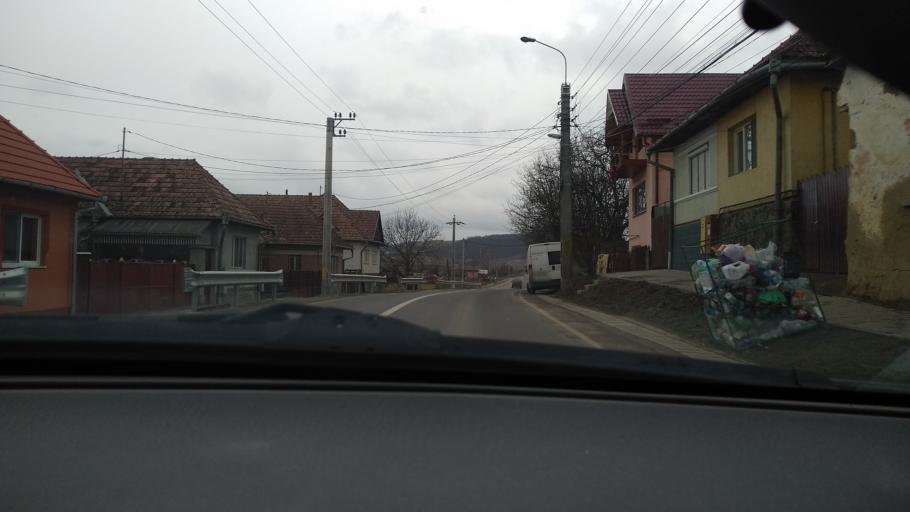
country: RO
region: Mures
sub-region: Comuna Miercurea Nirajului
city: Miercurea Nirajului
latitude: 46.5317
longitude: 24.7888
